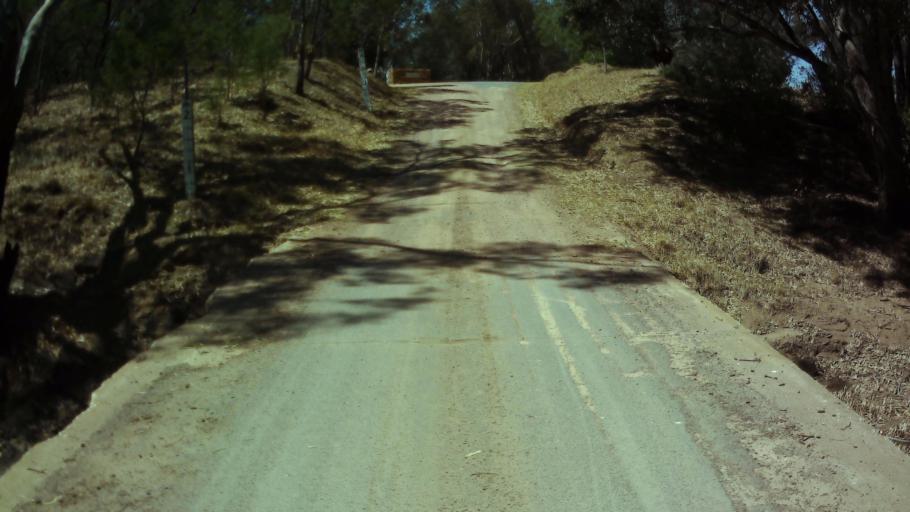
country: AU
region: New South Wales
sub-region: Weddin
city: Grenfell
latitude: -34.0322
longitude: 148.0136
